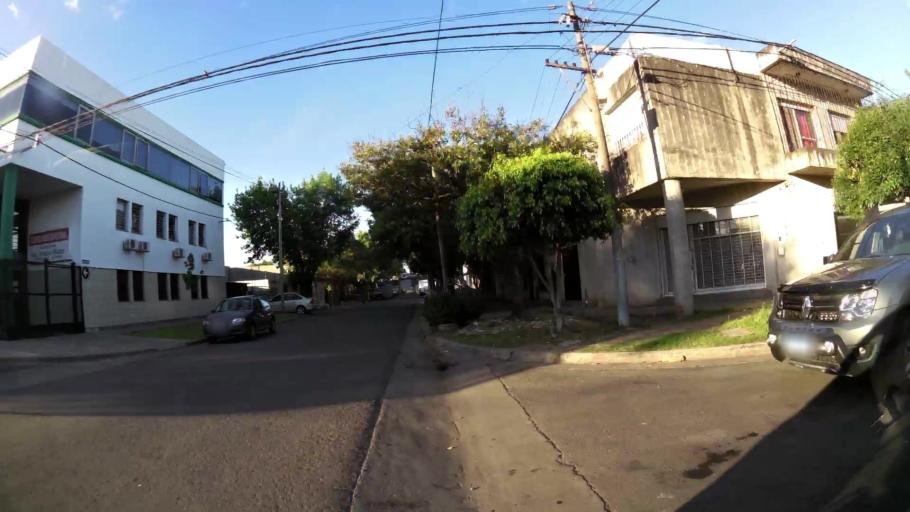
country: AR
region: Santa Fe
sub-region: Departamento de Rosario
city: Rosario
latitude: -32.9733
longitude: -60.6721
